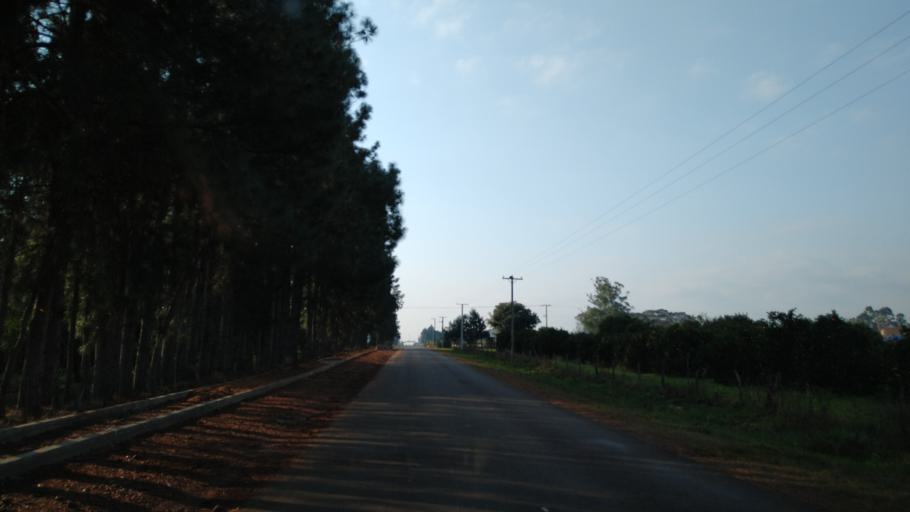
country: AR
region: Entre Rios
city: Santa Ana
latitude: -30.9058
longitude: -57.9254
